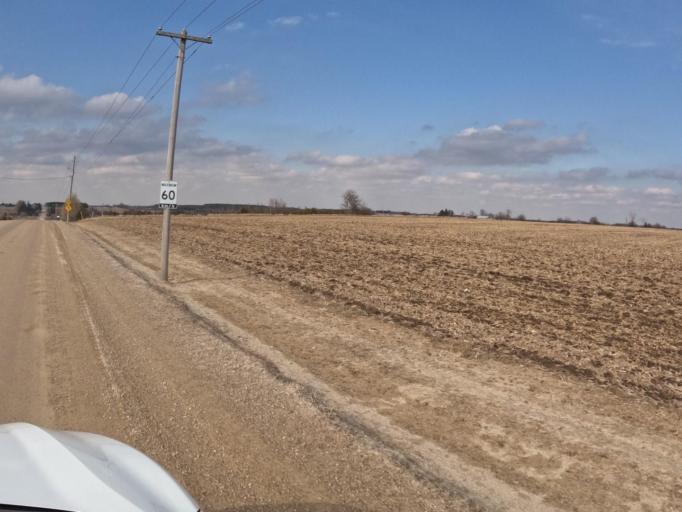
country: CA
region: Ontario
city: Orangeville
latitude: 43.8875
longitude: -80.2984
